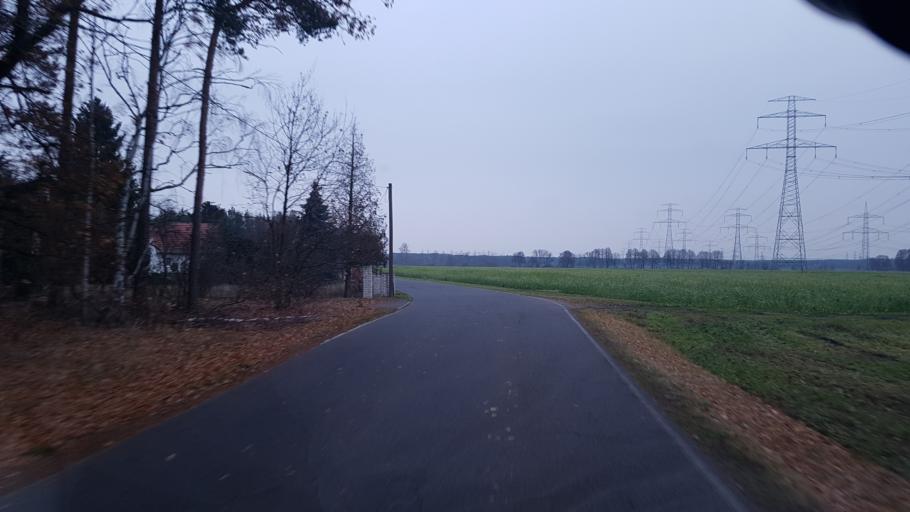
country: DE
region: Brandenburg
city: Peitz
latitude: 51.8806
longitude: 14.3992
